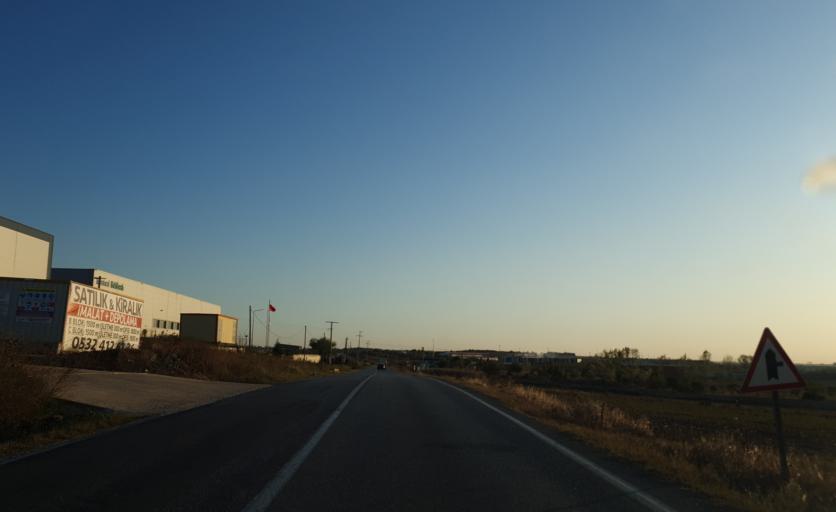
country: TR
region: Tekirdag
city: Beyazkoy
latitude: 41.3430
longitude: 27.7115
